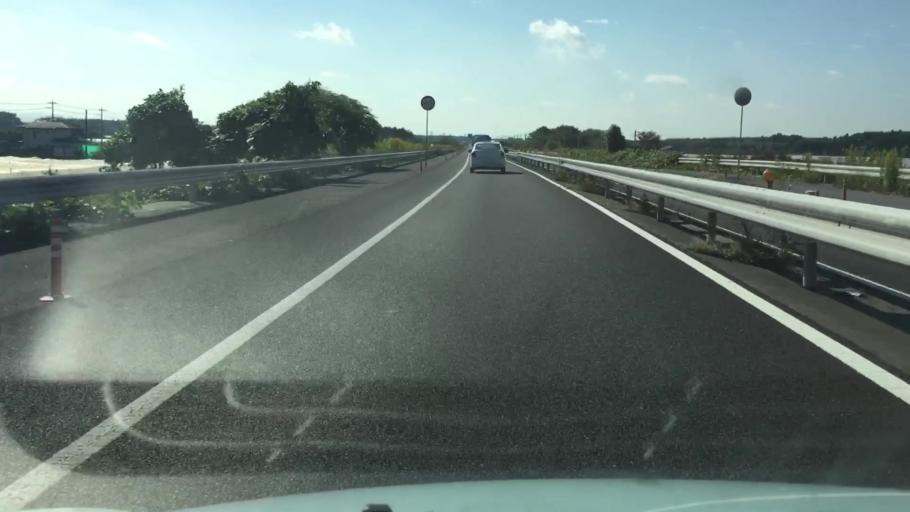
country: JP
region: Tochigi
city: Mooka
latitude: 36.5242
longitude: 139.9842
